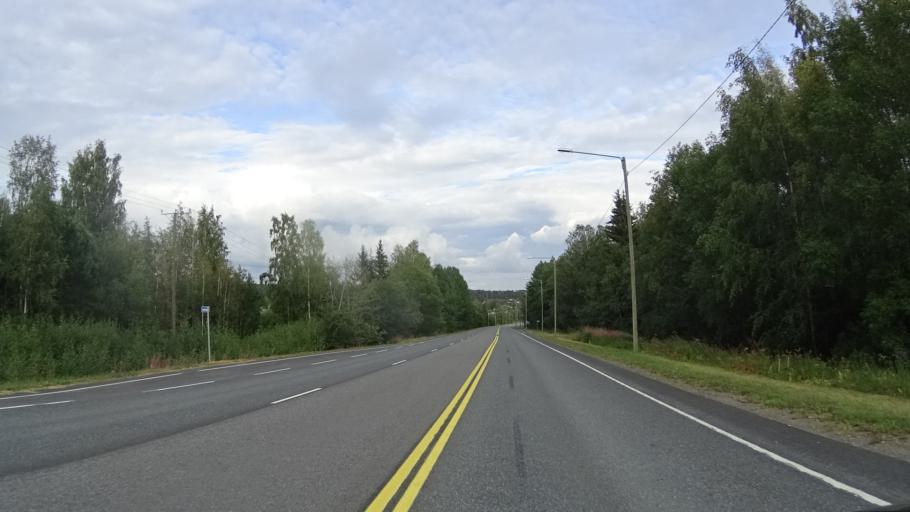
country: FI
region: Haeme
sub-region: Haemeenlinna
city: Parola
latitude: 61.0253
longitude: 24.3138
